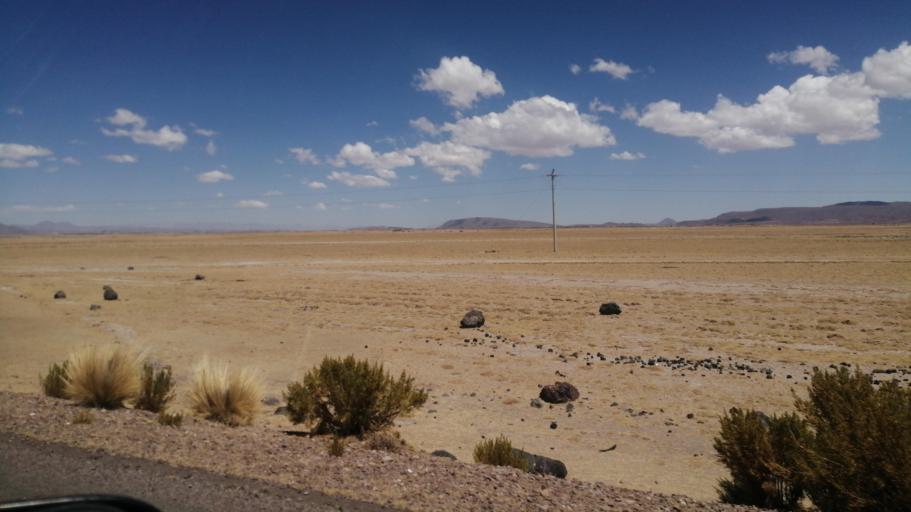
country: BO
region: Oruro
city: Challapata
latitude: -19.2186
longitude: -67.0014
